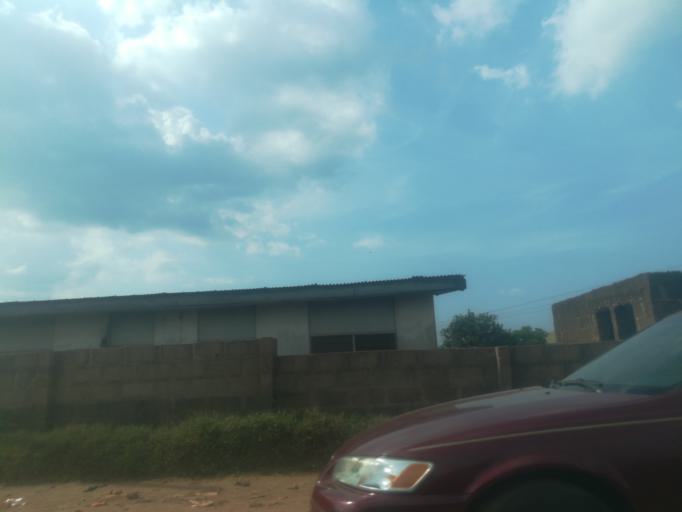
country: NG
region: Ogun
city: Abeokuta
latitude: 7.1183
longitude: 3.3181
